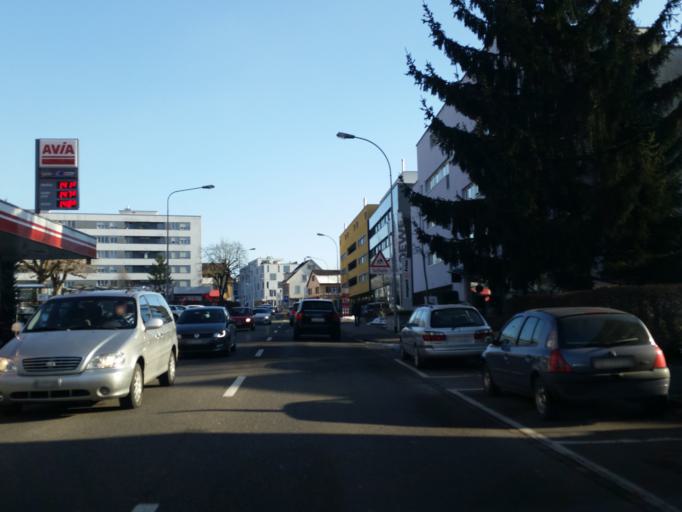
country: CH
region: Aargau
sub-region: Bezirk Baden
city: Neuenhof
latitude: 47.4643
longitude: 8.3299
